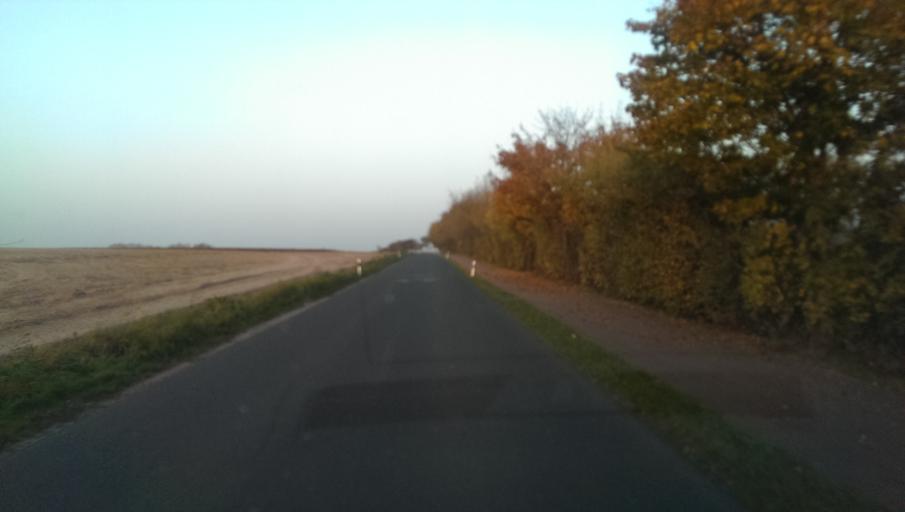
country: DE
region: Brandenburg
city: Juterbog
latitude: 51.9339
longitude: 13.0521
